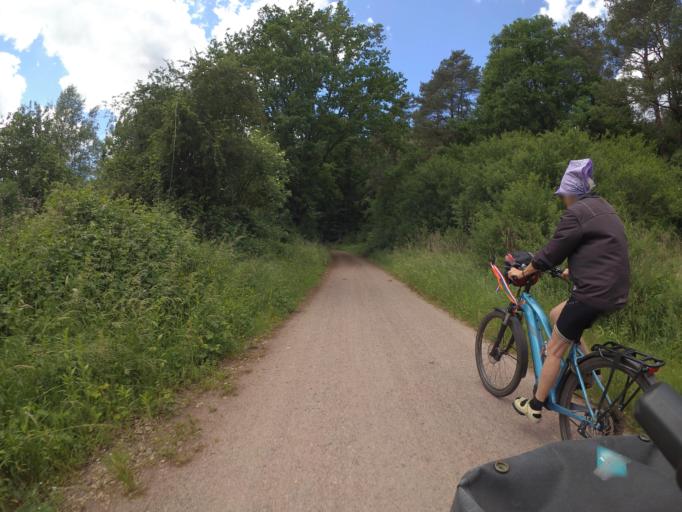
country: DE
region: Rheinland-Pfalz
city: Rumbach
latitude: 49.0827
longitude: 7.7534
